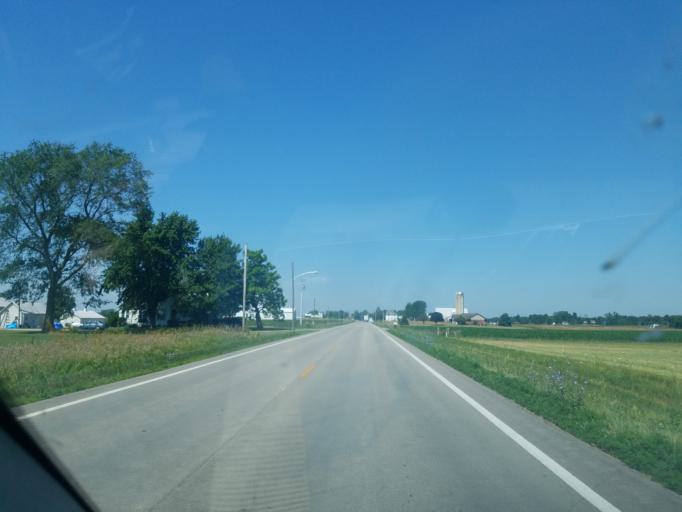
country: US
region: Ohio
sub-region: Shelby County
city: Botkins
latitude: 40.4390
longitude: -84.2513
